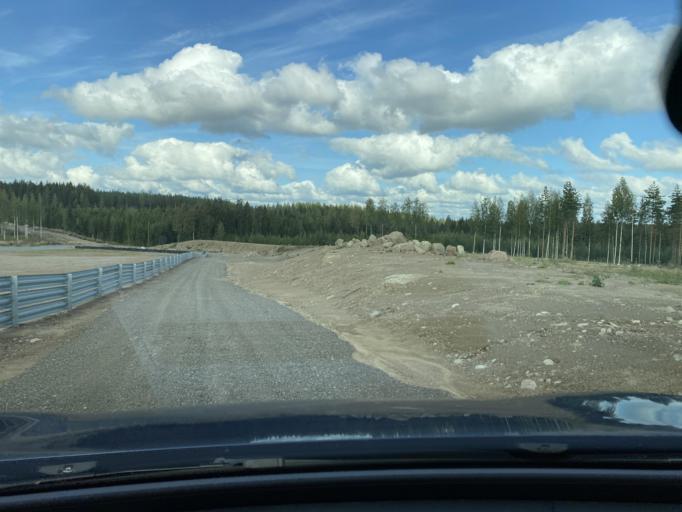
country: FI
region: Kymenlaakso
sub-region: Kouvola
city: Iitti
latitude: 60.8841
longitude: 26.4790
